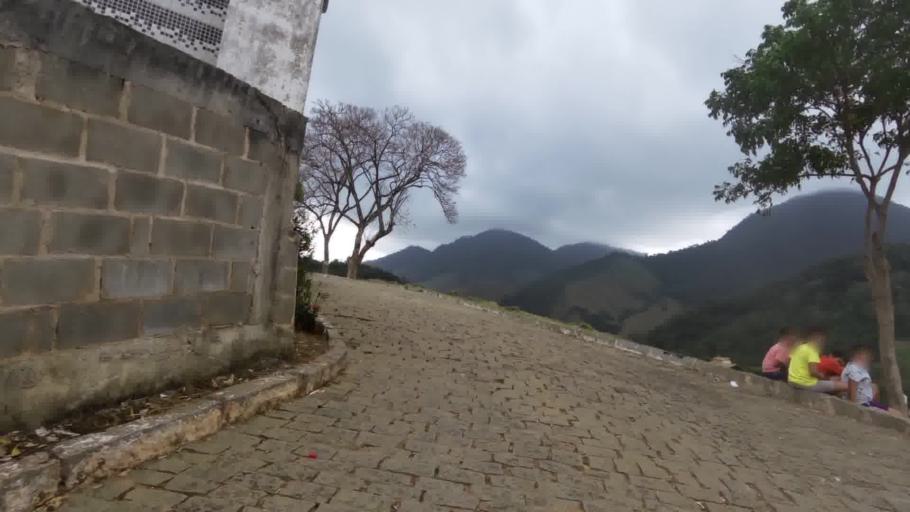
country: BR
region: Espirito Santo
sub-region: Alfredo Chaves
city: Alfredo Chaves
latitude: -20.6372
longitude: -40.7502
